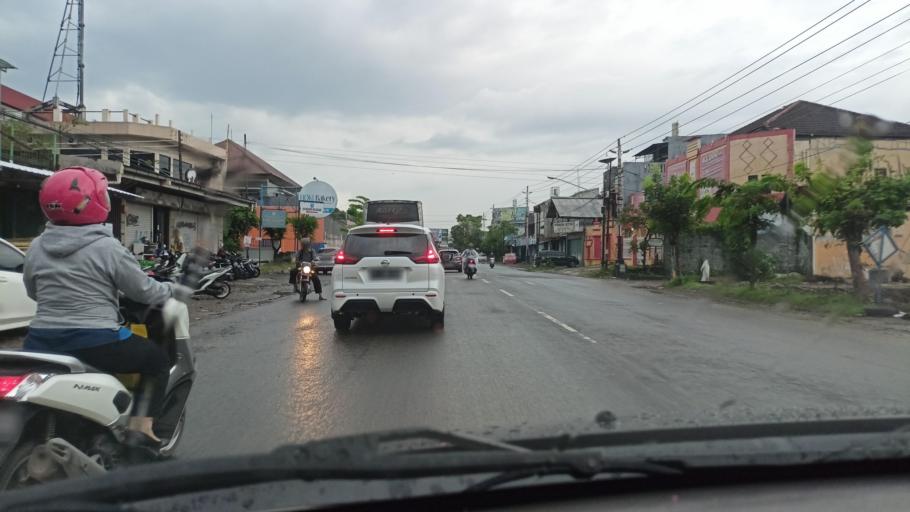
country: ID
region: Central Java
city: Surakarta
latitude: -7.5542
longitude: 110.8278
